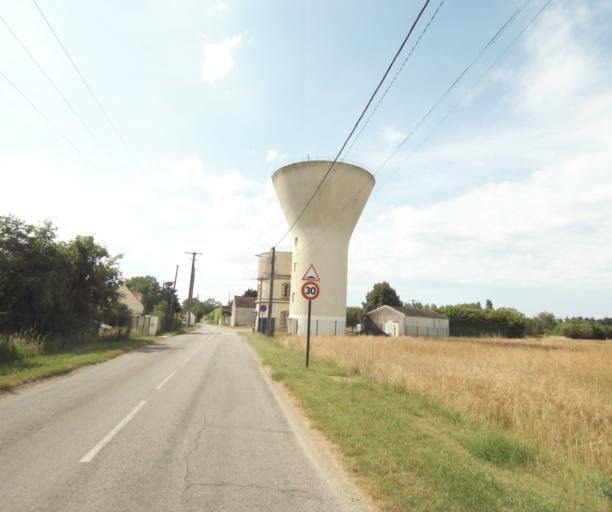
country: FR
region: Ile-de-France
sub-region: Departement de Seine-et-Marne
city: Acheres-la-Foret
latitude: 48.3525
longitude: 2.5735
